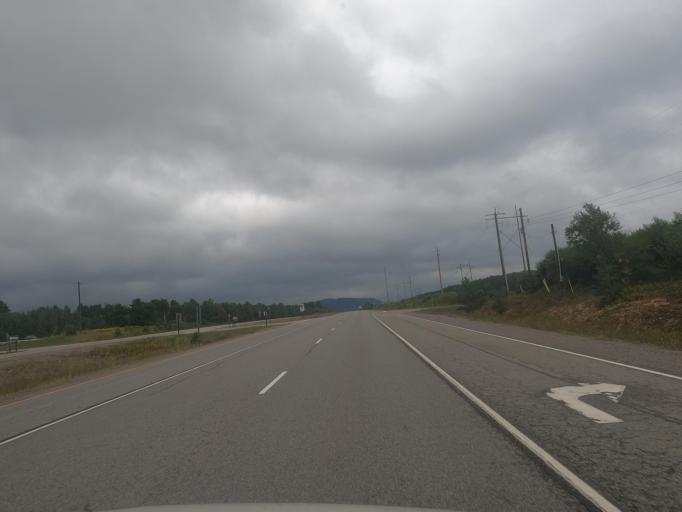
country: CA
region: Ontario
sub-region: Algoma
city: Sault Ste. Marie
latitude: 46.5577
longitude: -84.2122
